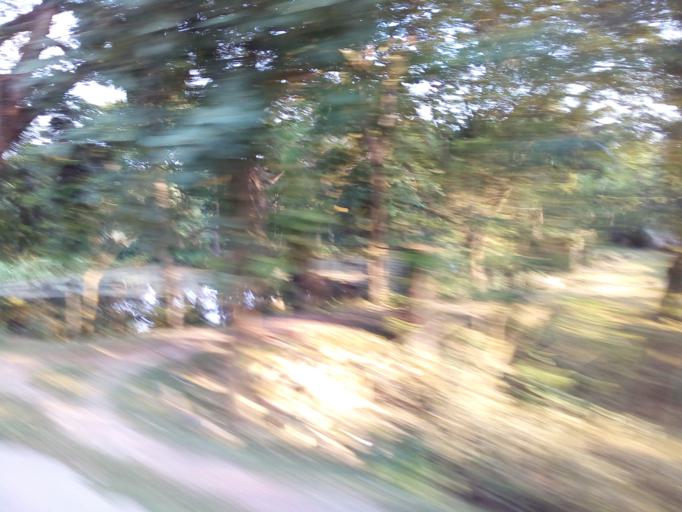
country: BD
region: Dhaka
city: Nagarpur
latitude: 23.8488
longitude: 89.8884
